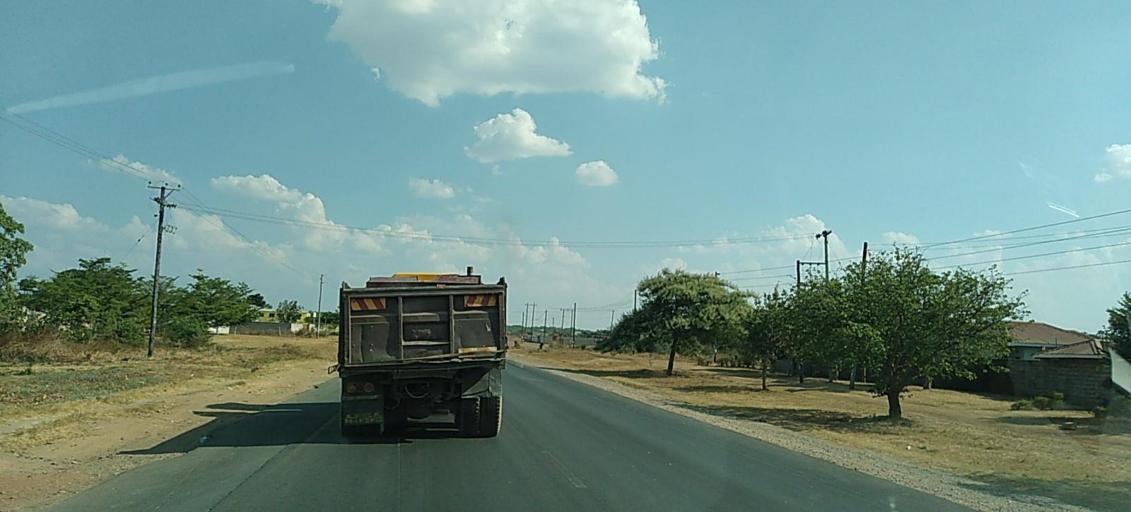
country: ZM
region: Lusaka
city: Lusaka
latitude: -15.2373
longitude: 28.2570
